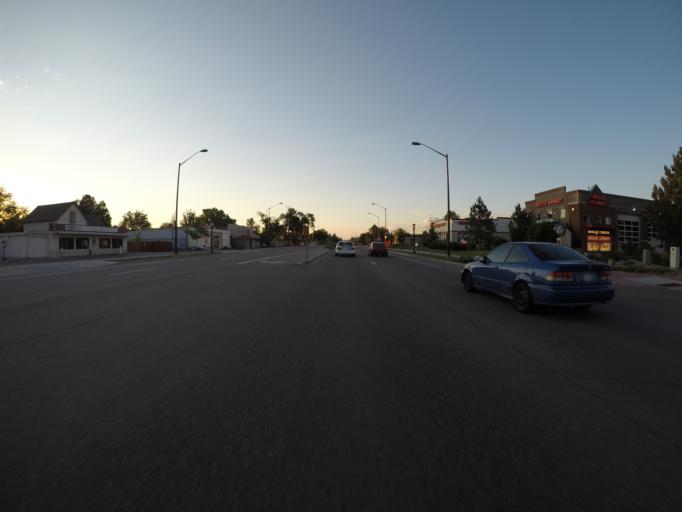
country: US
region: Colorado
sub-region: Larimer County
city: Fort Collins
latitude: 40.6071
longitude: -105.0765
